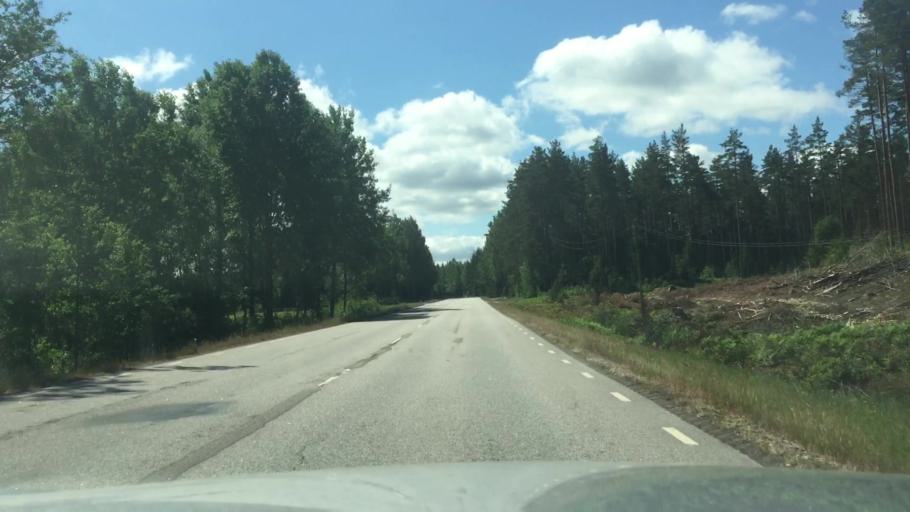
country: SE
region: Vaestra Goetaland
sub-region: Karlsborgs Kommun
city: Molltorp
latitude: 58.6243
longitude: 14.3887
